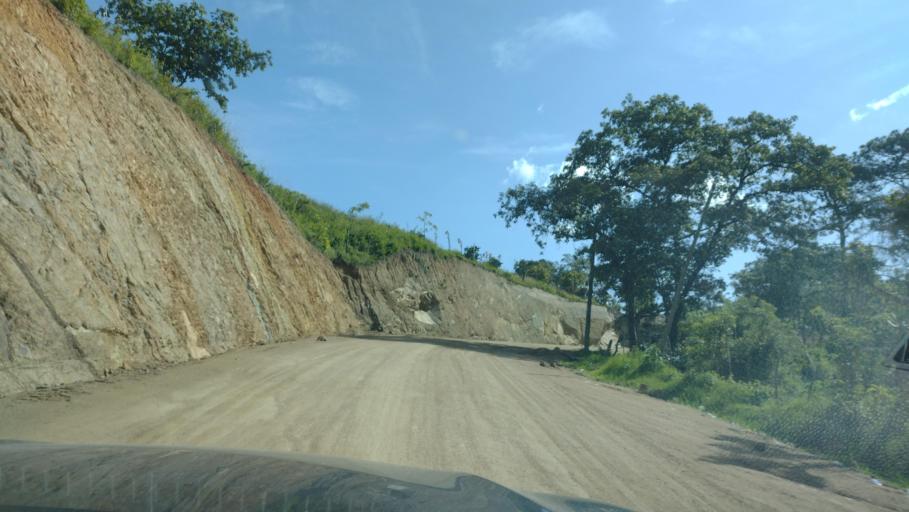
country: GT
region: Guatemala
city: Chinautla
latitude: 14.7534
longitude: -90.5109
